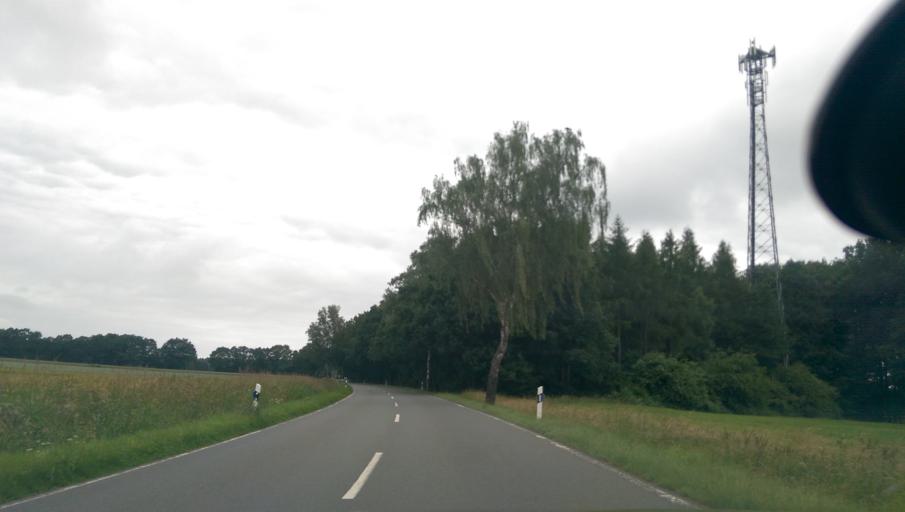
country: DE
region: Lower Saxony
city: Bomlitz
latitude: 52.9409
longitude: 9.6841
